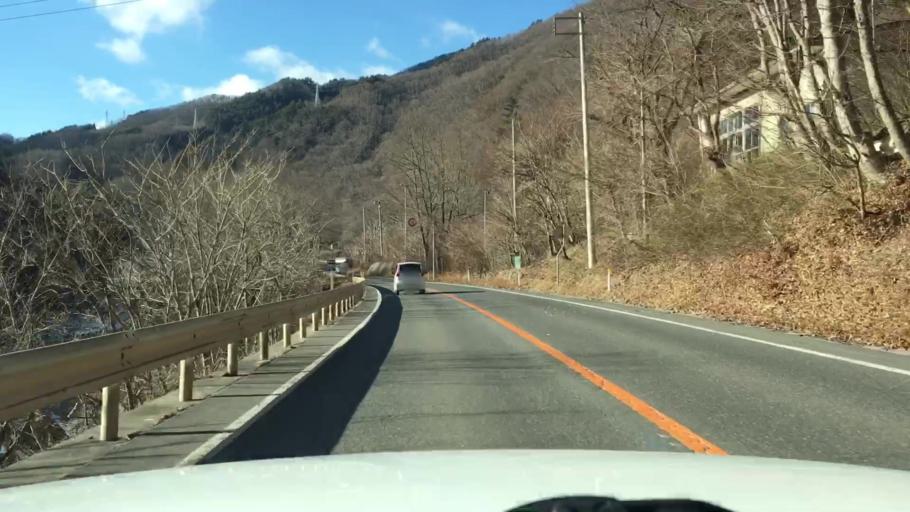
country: JP
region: Iwate
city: Miyako
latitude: 39.5985
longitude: 141.7387
